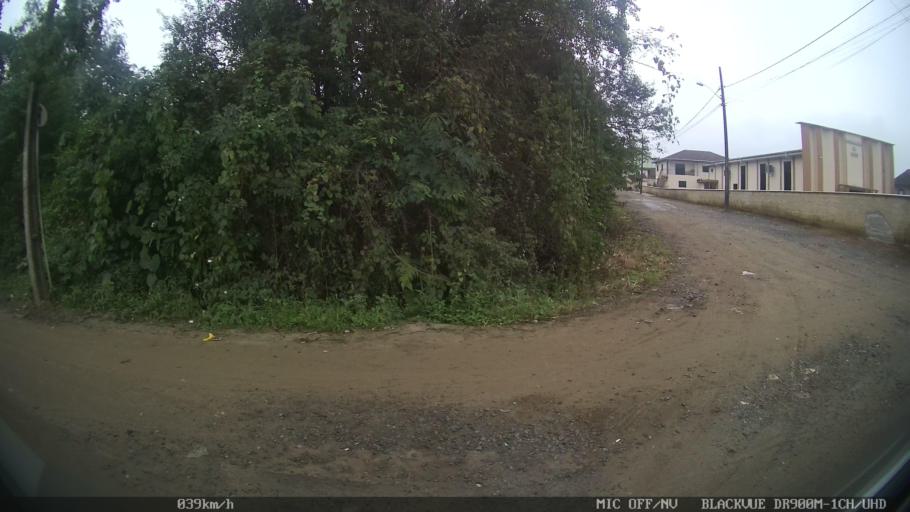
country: BR
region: Santa Catarina
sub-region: Joinville
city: Joinville
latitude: -26.2208
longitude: -48.8214
